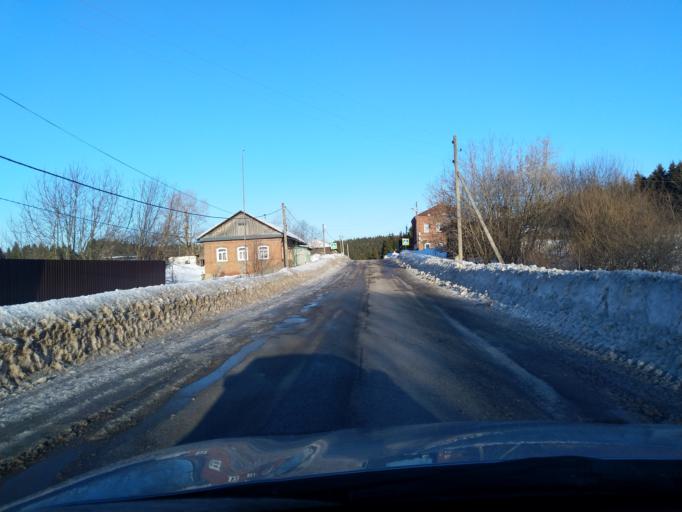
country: RU
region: Perm
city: Polazna
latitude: 58.3081
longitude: 56.4566
